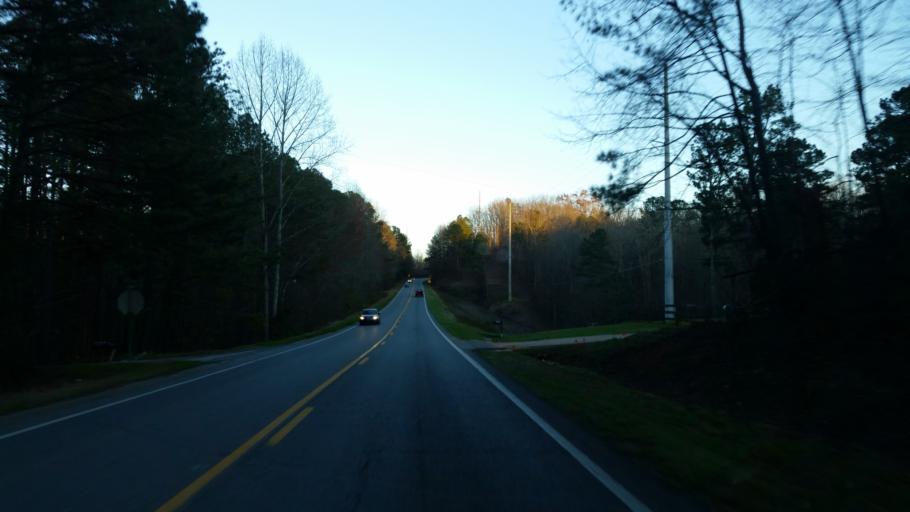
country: US
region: Georgia
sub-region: Dawson County
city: Dawsonville
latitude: 34.3327
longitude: -84.0158
